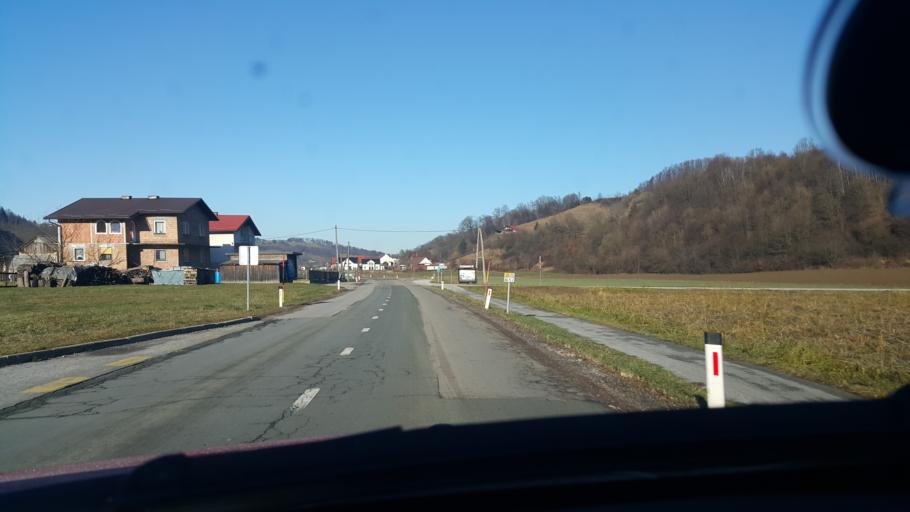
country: SI
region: Kungota
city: Zgornja Kungota
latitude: 46.6265
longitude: 15.6309
